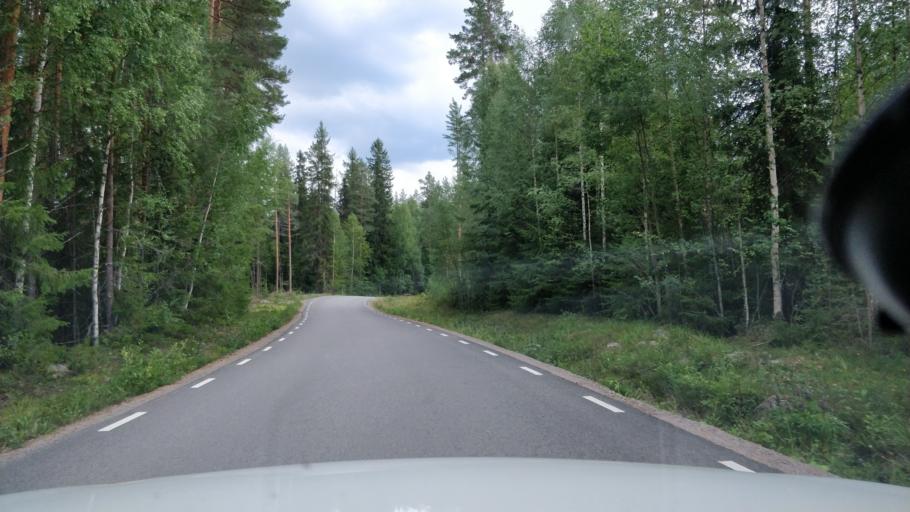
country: SE
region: Dalarna
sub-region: Faluns Kommun
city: Bjursas
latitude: 60.7492
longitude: 15.5275
